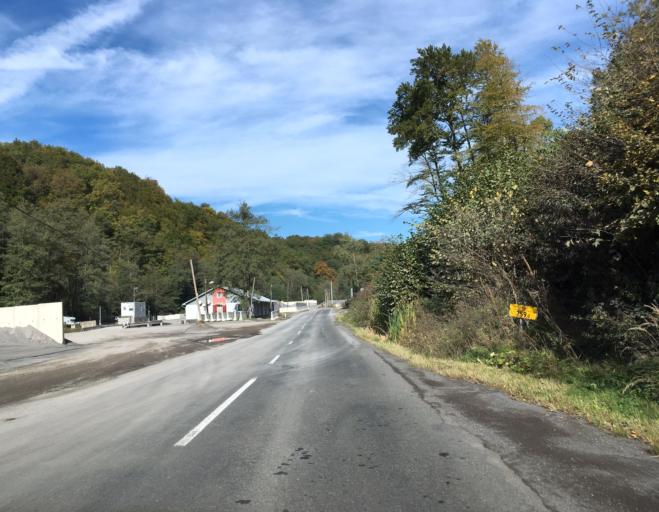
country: SK
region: Banskobystricky
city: Krupina
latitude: 48.3221
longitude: 18.9775
